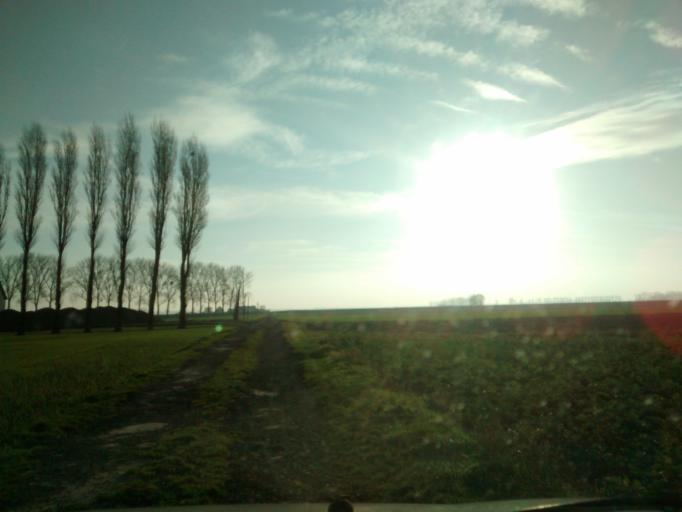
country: FR
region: Brittany
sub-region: Departement d'Ille-et-Vilaine
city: Roz-sur-Couesnon
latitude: 48.6130
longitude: -1.5568
